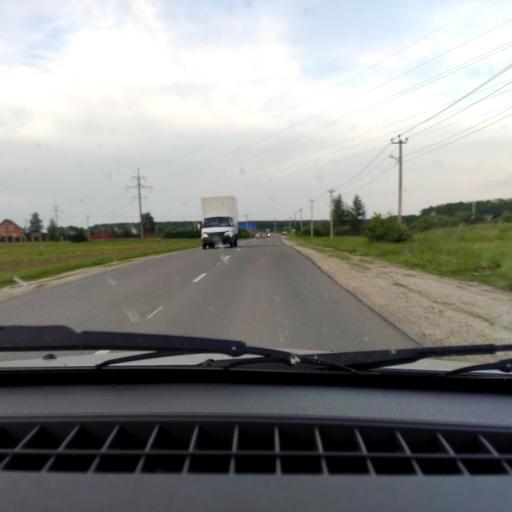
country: RU
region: Voronezj
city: Ramon'
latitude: 51.9511
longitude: 39.3906
